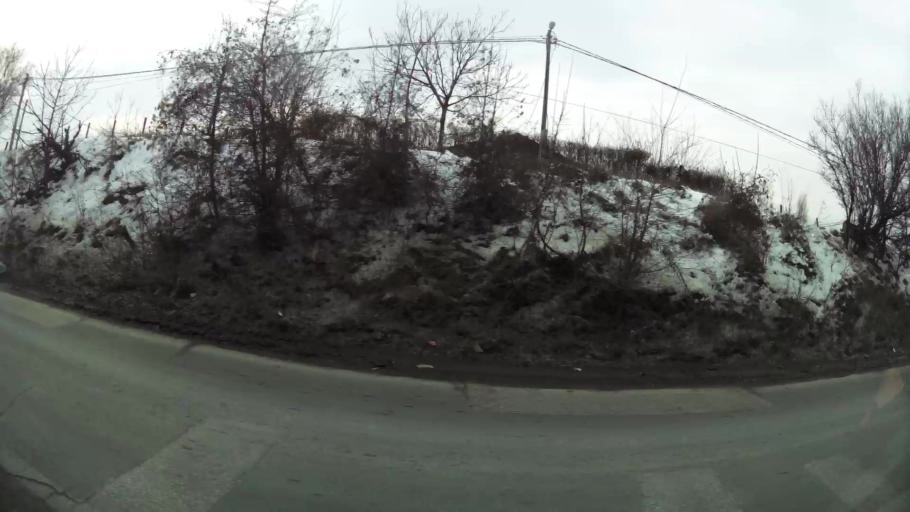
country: MK
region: Suto Orizari
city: Suto Orizare
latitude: 42.0307
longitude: 21.4057
